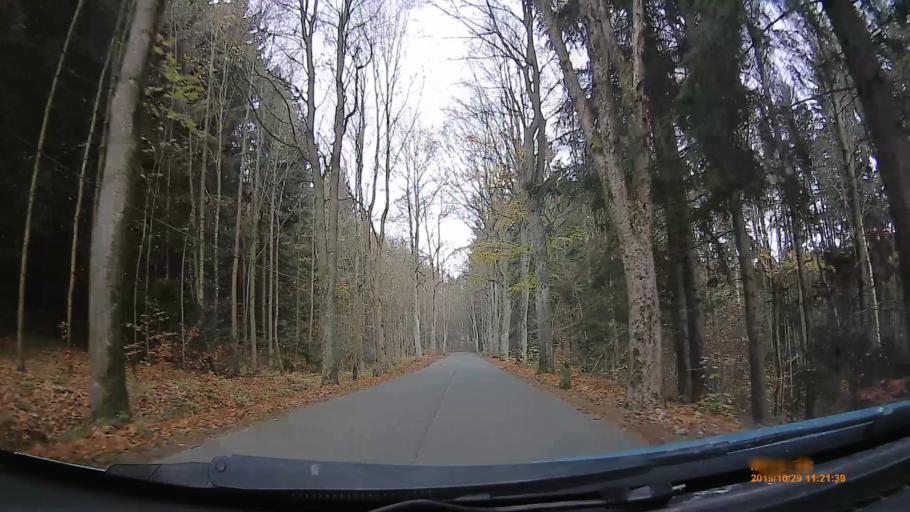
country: PL
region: Lower Silesian Voivodeship
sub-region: Powiat klodzki
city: Szczytna
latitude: 50.4304
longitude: 16.4385
